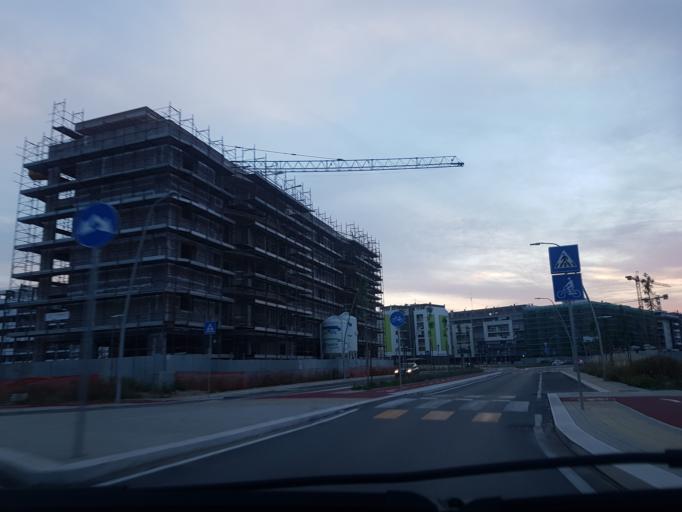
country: IT
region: Apulia
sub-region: Provincia di Barletta - Andria - Trani
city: Barletta
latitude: 41.3048
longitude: 16.2701
